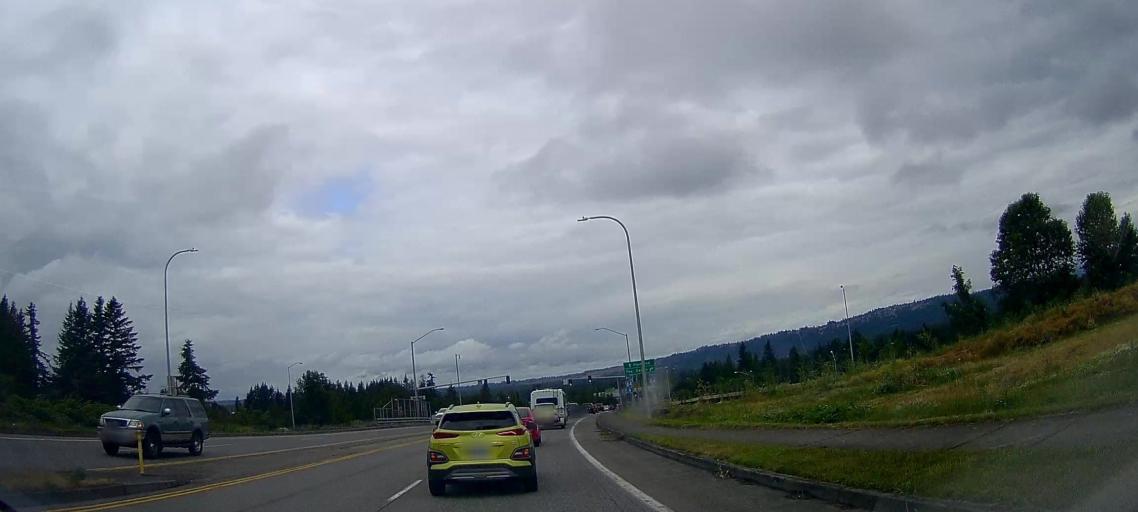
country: US
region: Oregon
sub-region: Multnomah County
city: Fairview
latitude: 45.5379
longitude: -122.4483
